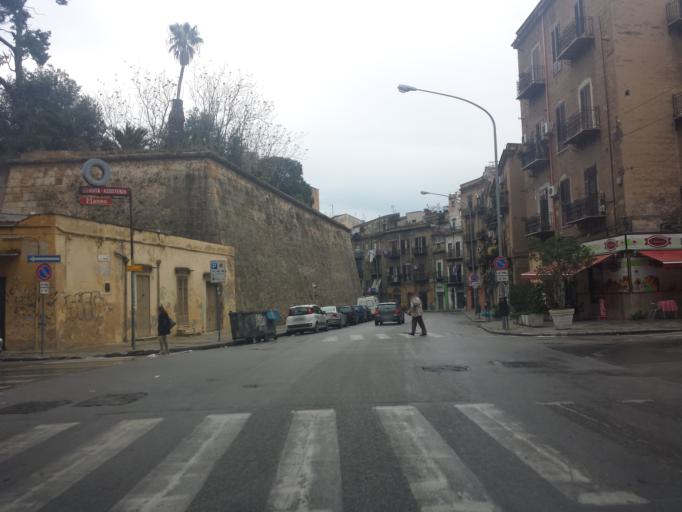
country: IT
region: Sicily
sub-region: Palermo
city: Palermo
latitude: 38.1174
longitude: 13.3509
